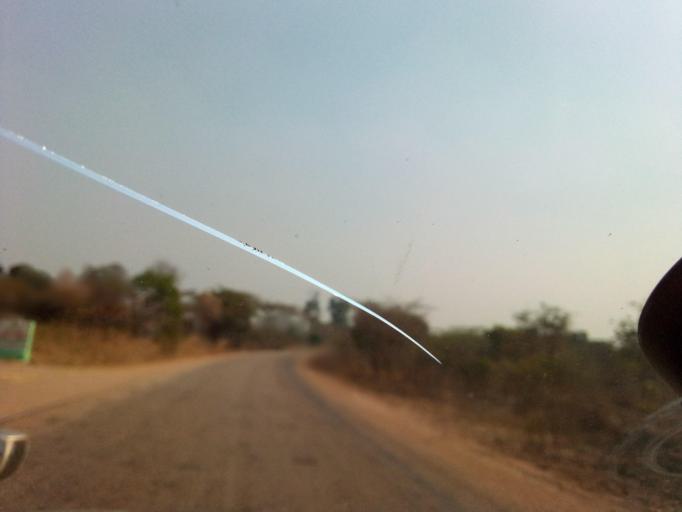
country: ZM
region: Northern
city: Chinsali
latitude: -10.9317
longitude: 32.0423
